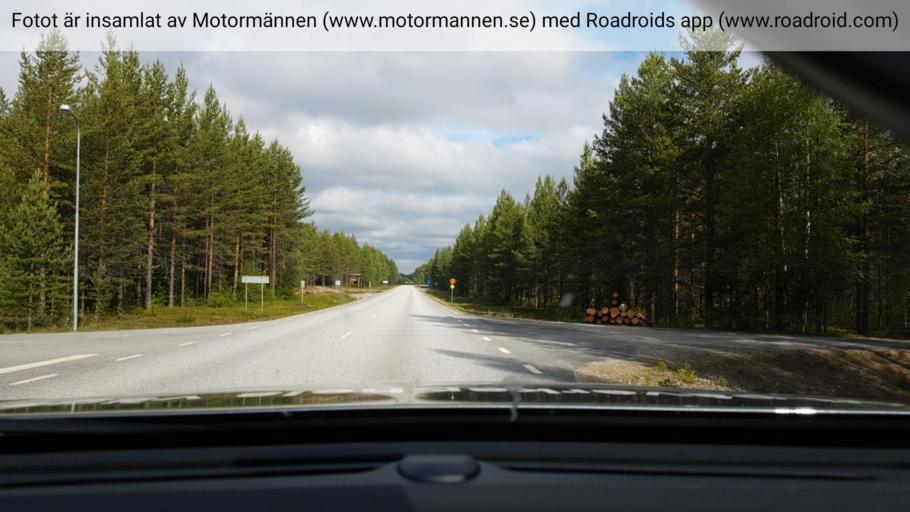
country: SE
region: Vaesterbotten
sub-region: Vindelns Kommun
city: Vindeln
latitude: 64.3820
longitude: 19.3885
